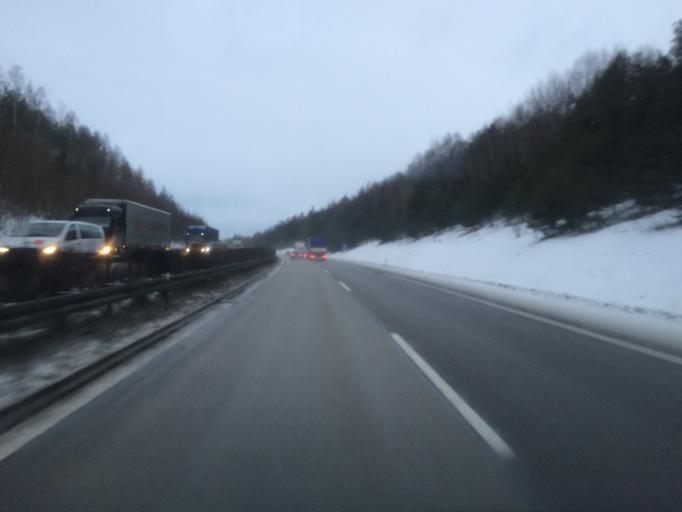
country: DE
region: Bavaria
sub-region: Upper Palatinate
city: Zeitlarn
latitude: 49.0828
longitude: 12.1007
